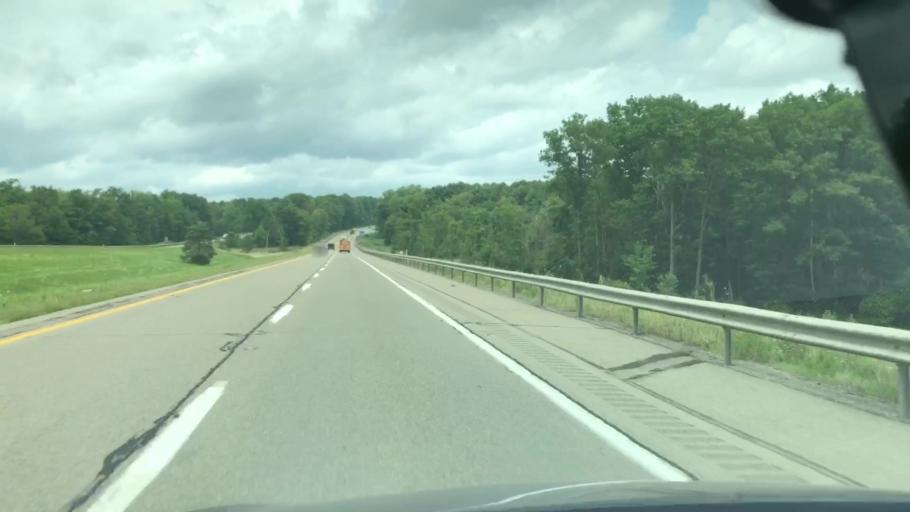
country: US
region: Pennsylvania
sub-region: Erie County
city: Edinboro
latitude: 41.8337
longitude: -80.1754
